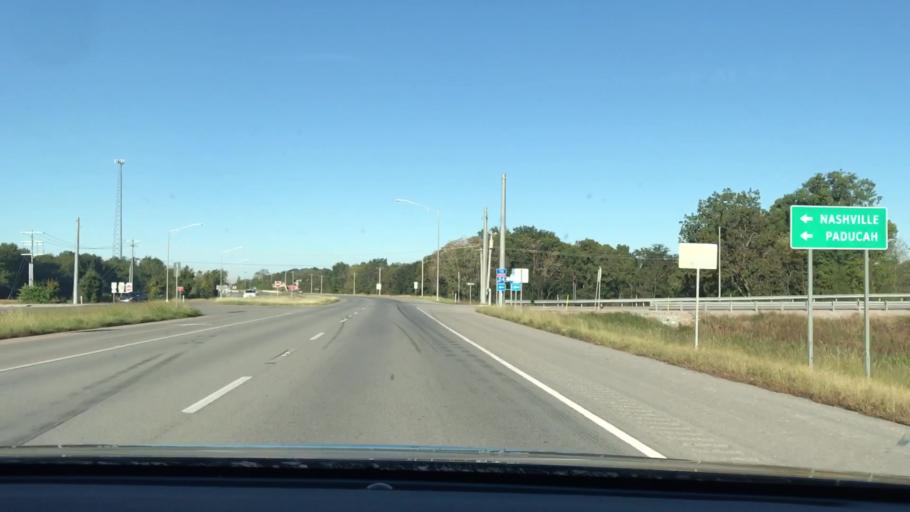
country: US
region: Kentucky
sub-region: Christian County
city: Hopkinsville
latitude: 36.8183
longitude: -87.4837
